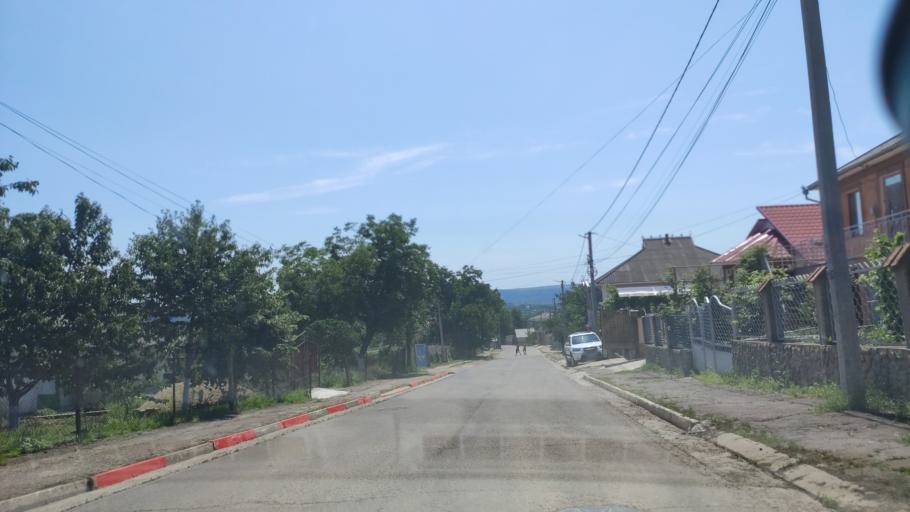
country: MD
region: Raionul Soroca
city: Soroca
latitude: 48.1703
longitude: 28.2984
